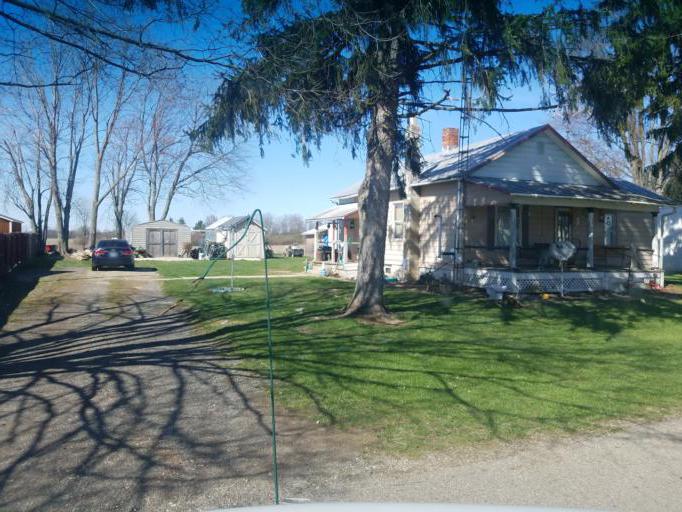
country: US
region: Ohio
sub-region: Morrow County
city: Mount Gilead
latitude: 40.5614
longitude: -82.8660
